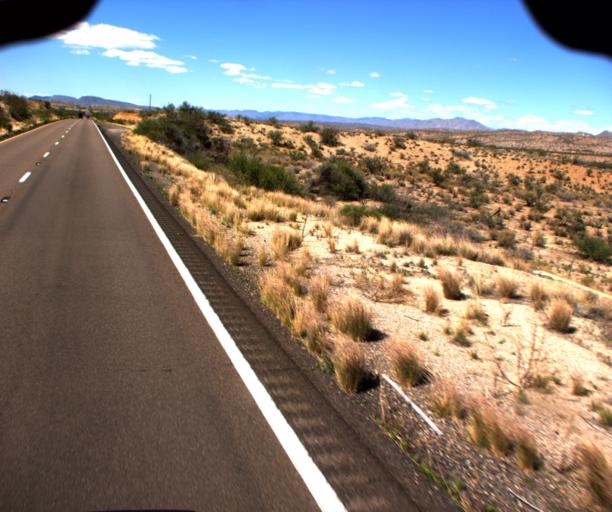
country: US
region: Arizona
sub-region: Mohave County
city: Kingman
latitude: 35.0308
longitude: -113.6643
